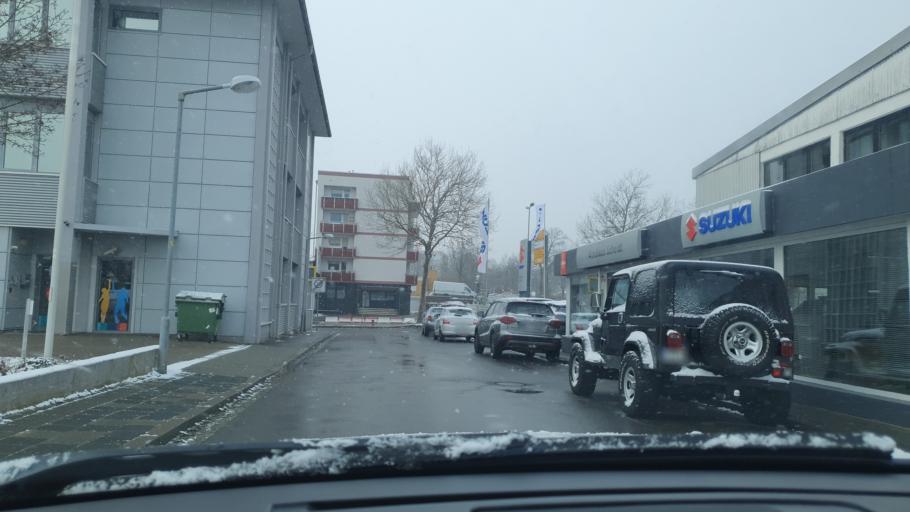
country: DE
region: Rheinland-Pfalz
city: Kaiserslautern
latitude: 49.4544
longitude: 7.7947
